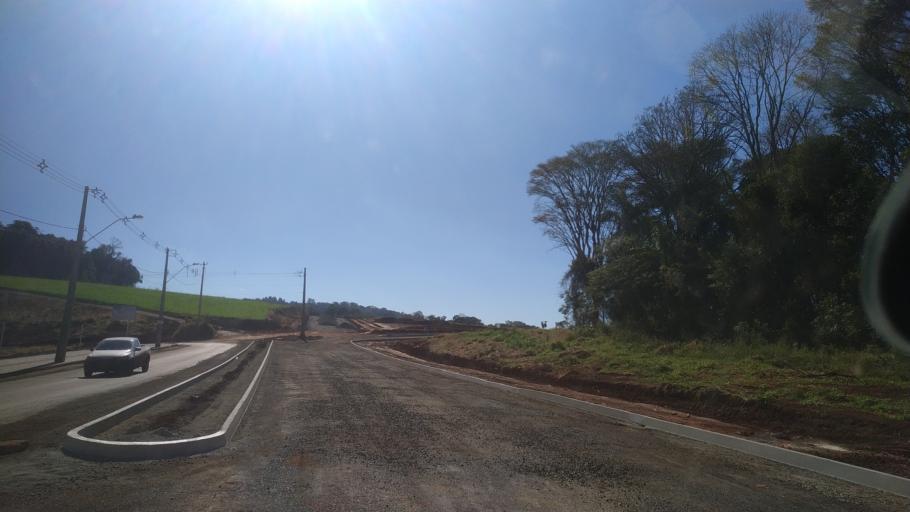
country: BR
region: Santa Catarina
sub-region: Chapeco
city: Chapeco
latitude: -27.0858
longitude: -52.6916
